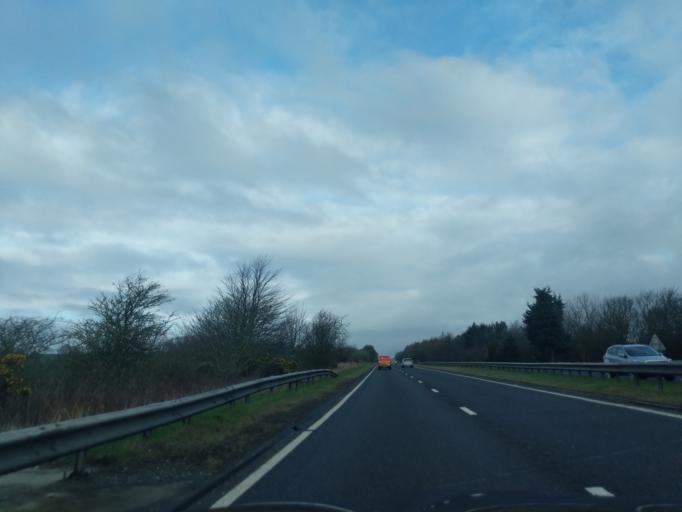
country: GB
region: England
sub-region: Northumberland
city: Morpeth
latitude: 55.1376
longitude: -1.6819
